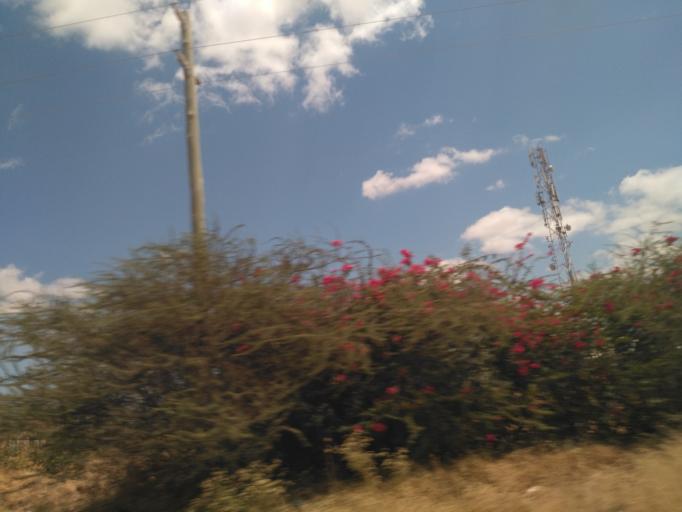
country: TZ
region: Dodoma
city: Kisasa
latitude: -6.1659
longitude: 35.7908
